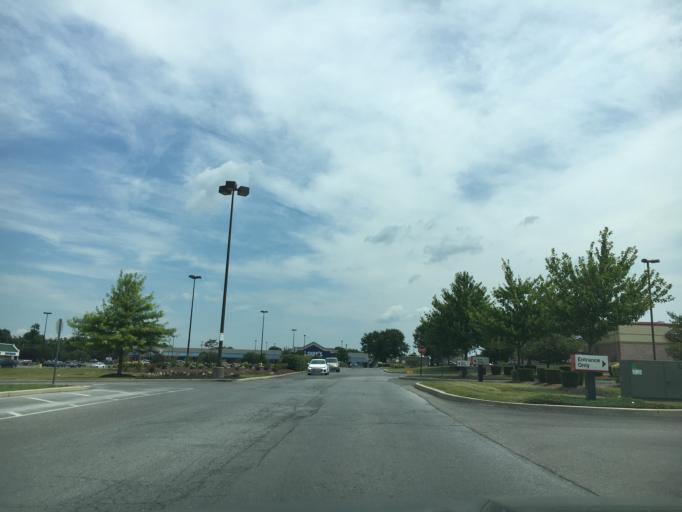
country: US
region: Maryland
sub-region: Washington County
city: Halfway
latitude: 39.6315
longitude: -77.7627
